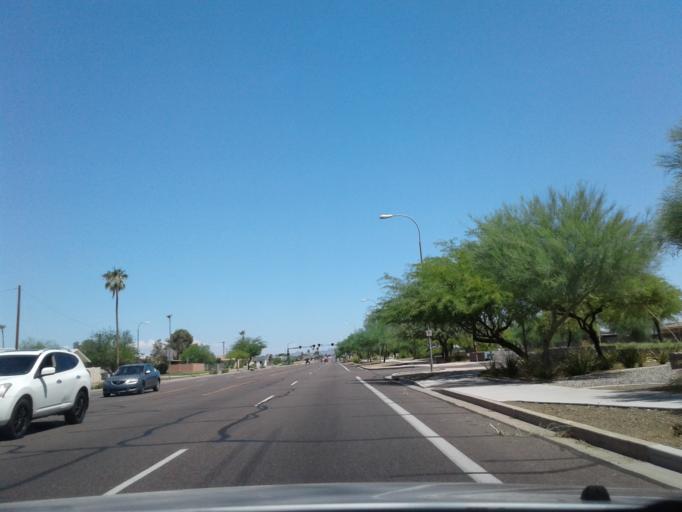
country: US
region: Arizona
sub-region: Maricopa County
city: Phoenix
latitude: 33.4009
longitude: -112.0298
